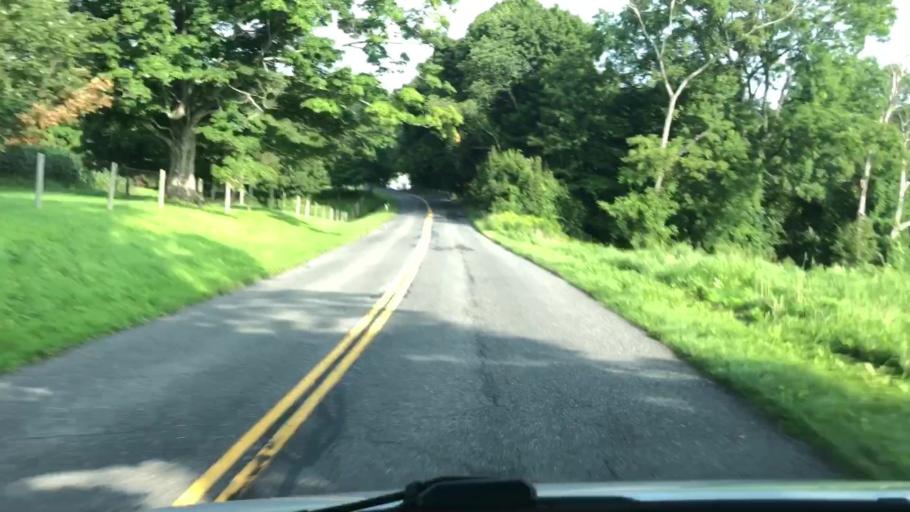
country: US
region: Massachusetts
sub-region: Berkshire County
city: Lee
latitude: 42.3207
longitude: -73.2744
